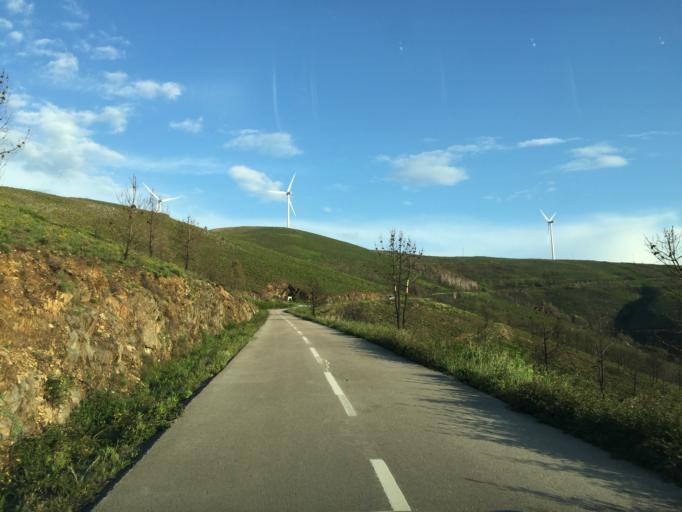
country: PT
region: Coimbra
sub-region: Pampilhosa da Serra
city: Pampilhosa da Serra
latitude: 40.1223
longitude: -8.0127
